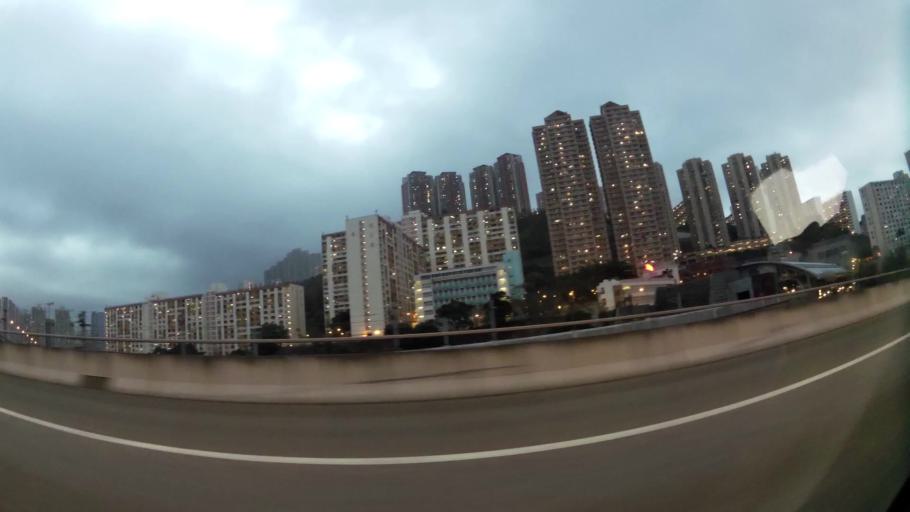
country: HK
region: Tsuen Wan
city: Tsuen Wan
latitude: 22.3496
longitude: 114.1245
